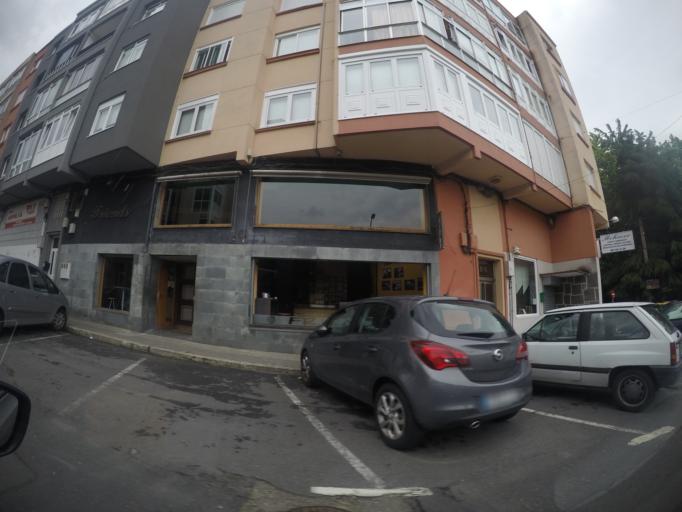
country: ES
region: Galicia
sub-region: Provincia da Coruna
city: Culleredo
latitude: 43.3078
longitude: -8.3832
